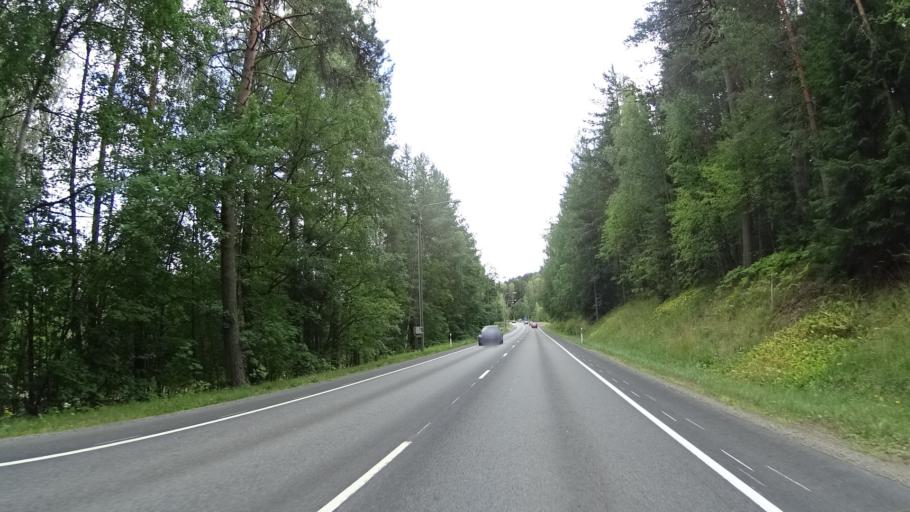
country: FI
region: Pirkanmaa
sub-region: Tampere
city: Kangasala
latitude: 61.4228
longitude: 24.1390
